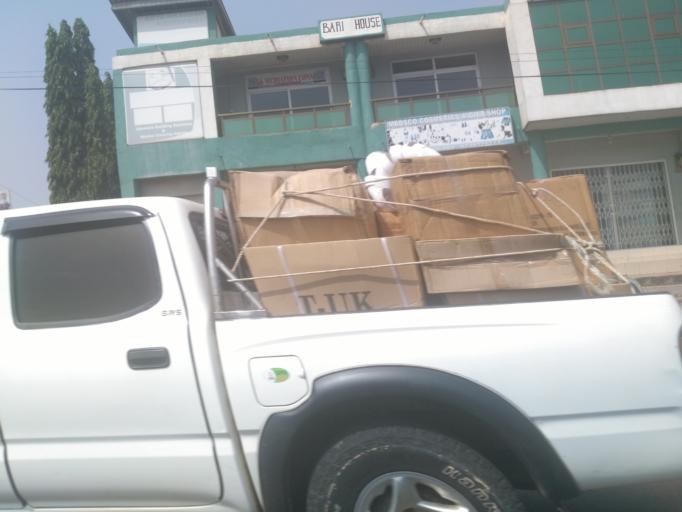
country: GH
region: Greater Accra
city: Dome
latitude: 5.6097
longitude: -0.2372
